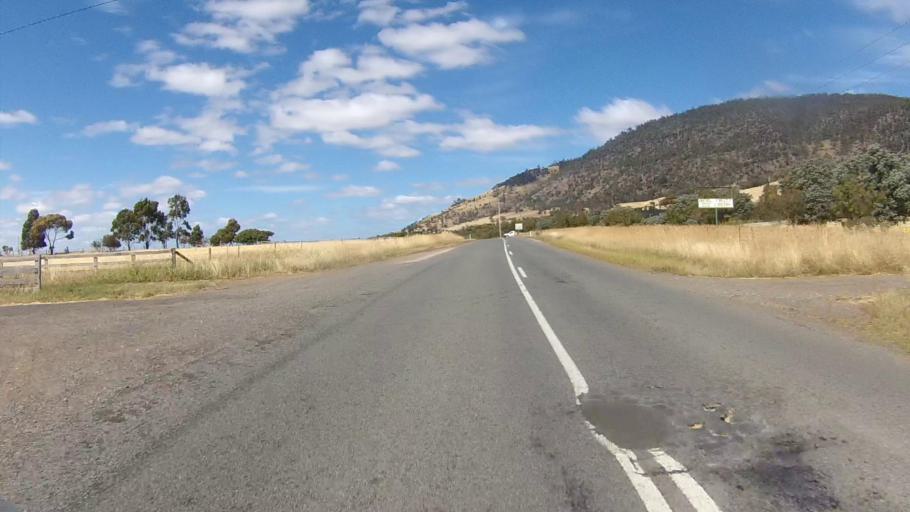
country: AU
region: Tasmania
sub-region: Sorell
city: Sorell
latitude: -42.6229
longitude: 147.4293
